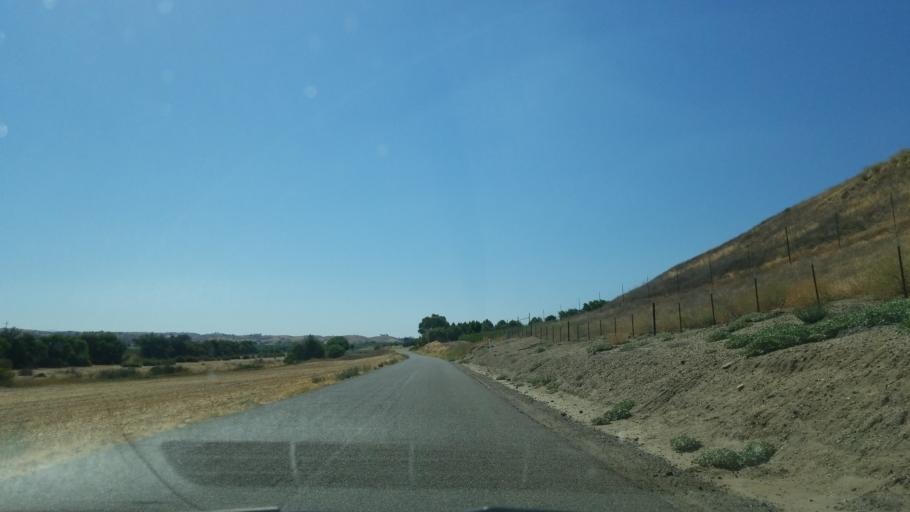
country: US
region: California
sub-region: San Luis Obispo County
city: San Miguel
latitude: 35.7322
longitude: -120.6616
